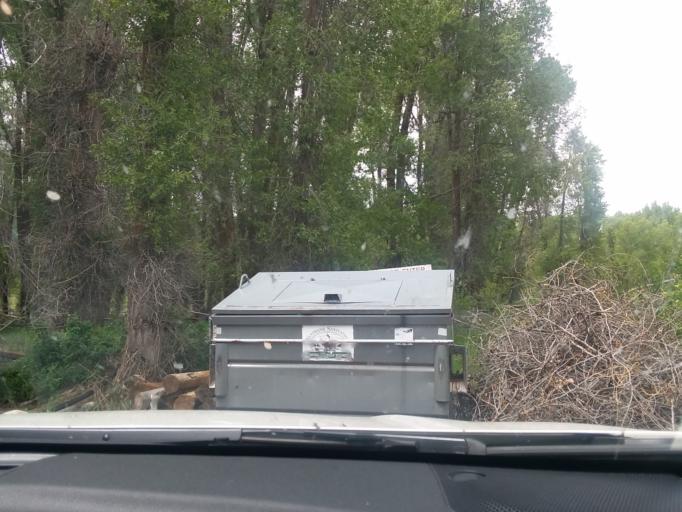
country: US
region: Wyoming
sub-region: Teton County
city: Moose Wilson Road
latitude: 43.5037
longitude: -110.8434
